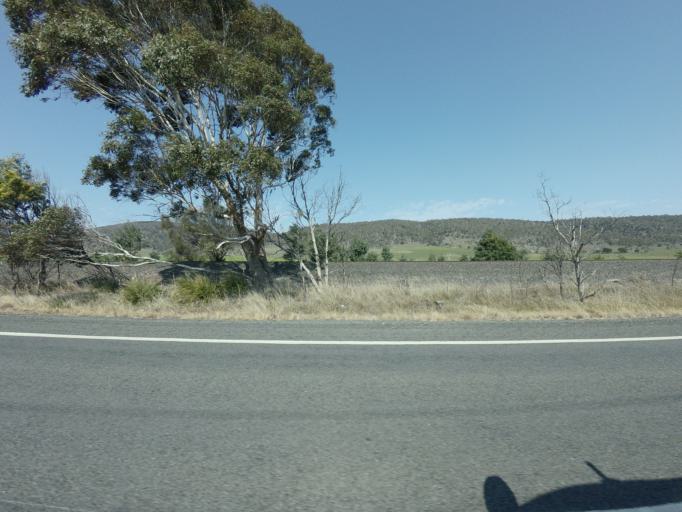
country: AU
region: Tasmania
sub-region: Northern Midlands
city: Evandale
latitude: -41.8112
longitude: 147.6240
